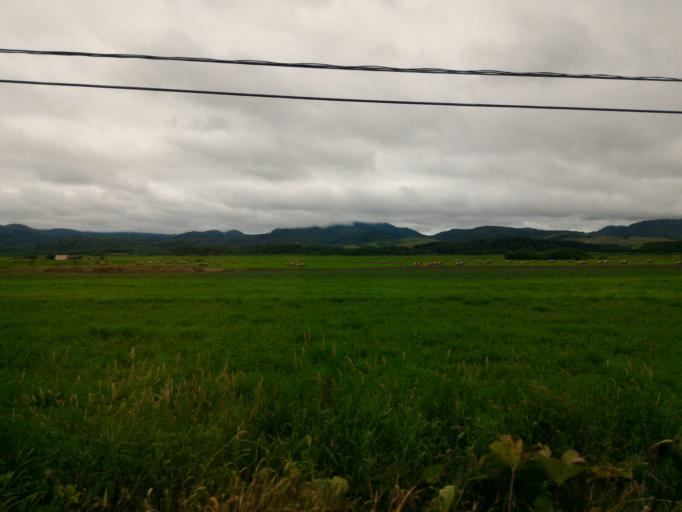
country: JP
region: Hokkaido
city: Makubetsu
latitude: 44.8277
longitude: 142.0623
